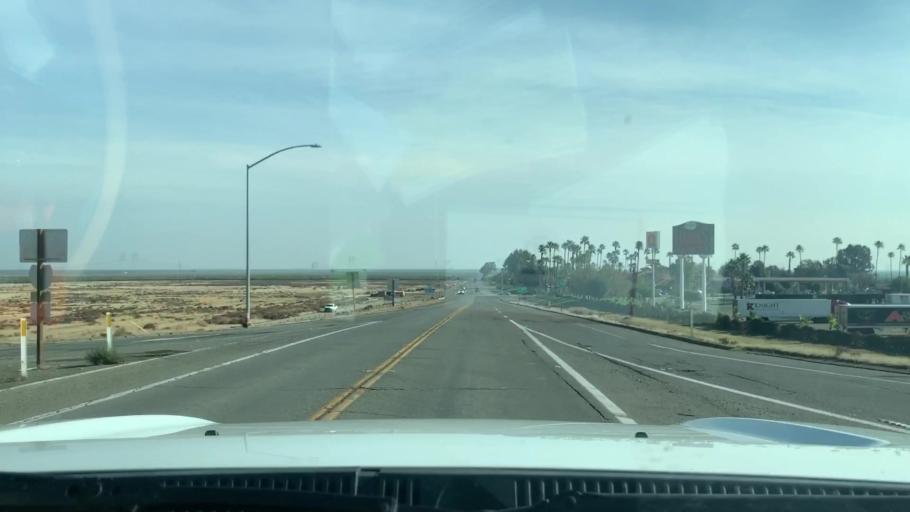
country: US
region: California
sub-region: Fresno County
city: Huron
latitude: 36.2544
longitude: -120.2416
